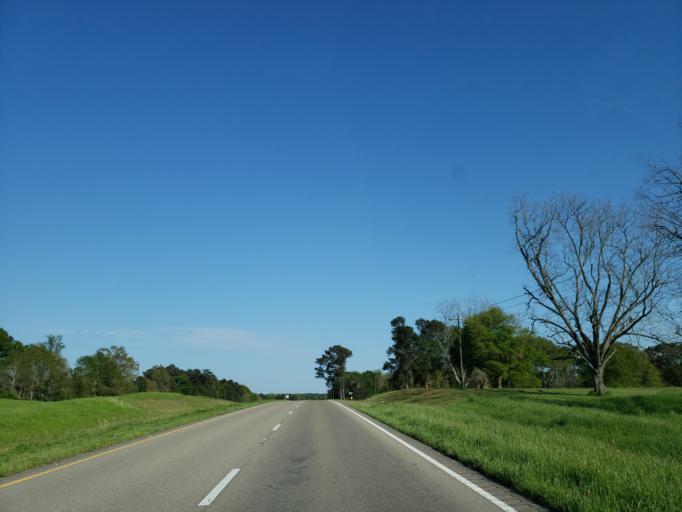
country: US
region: Mississippi
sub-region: Jones County
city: Ellisville
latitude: 31.6874
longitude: -89.3244
